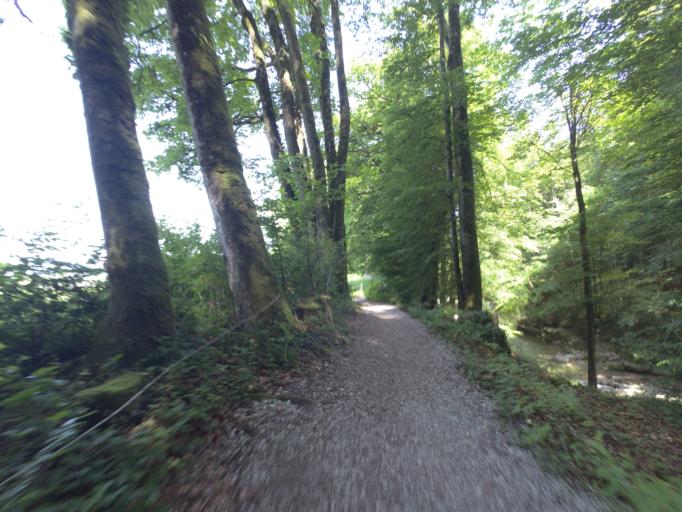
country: AT
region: Salzburg
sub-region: Politischer Bezirk Salzburg-Umgebung
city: Elsbethen
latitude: 47.7675
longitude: 13.0942
